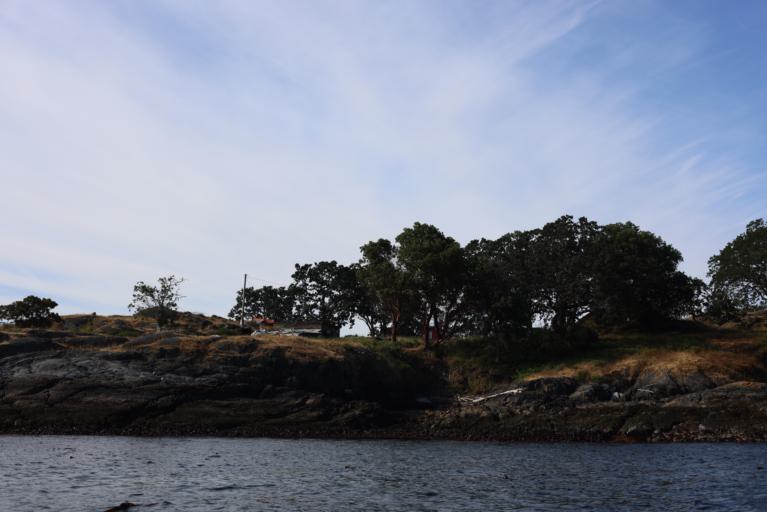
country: CA
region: British Columbia
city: Metchosin
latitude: 48.3414
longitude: -123.5282
